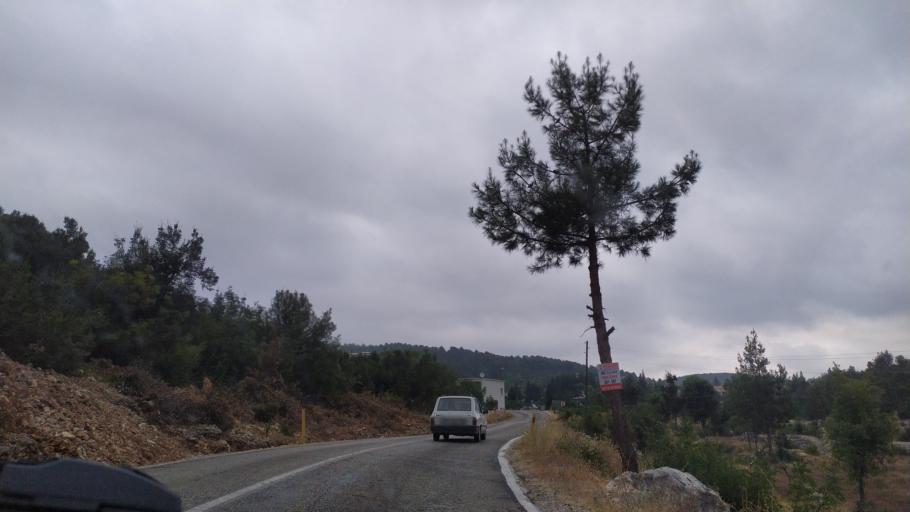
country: TR
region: Mersin
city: Silifke
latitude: 36.5348
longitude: 33.9421
